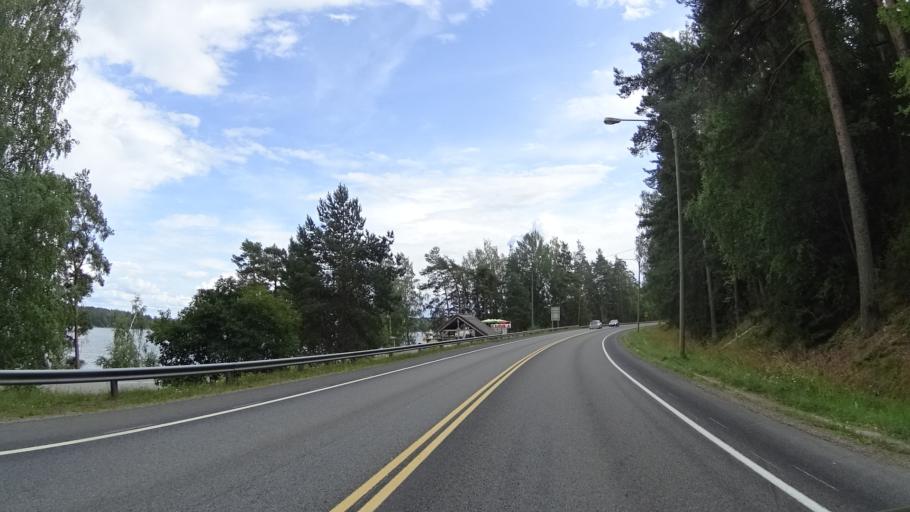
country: FI
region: Pirkanmaa
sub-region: Tampere
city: Kangasala
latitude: 61.4188
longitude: 24.1452
